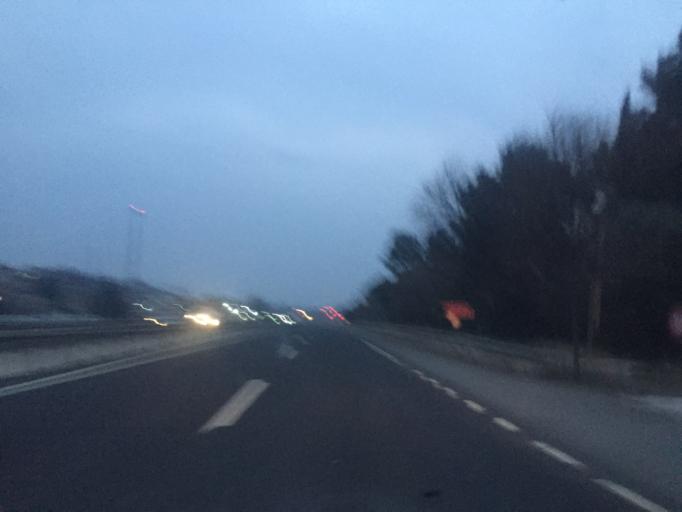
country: TR
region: Sanliurfa
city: Camlidere
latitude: 37.1546
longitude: 39.0611
